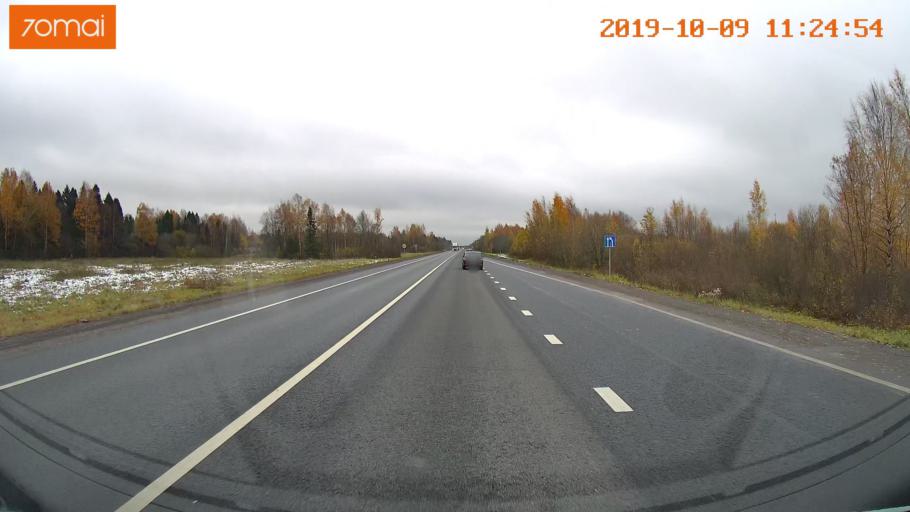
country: RU
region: Vologda
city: Vologda
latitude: 59.1068
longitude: 39.9852
